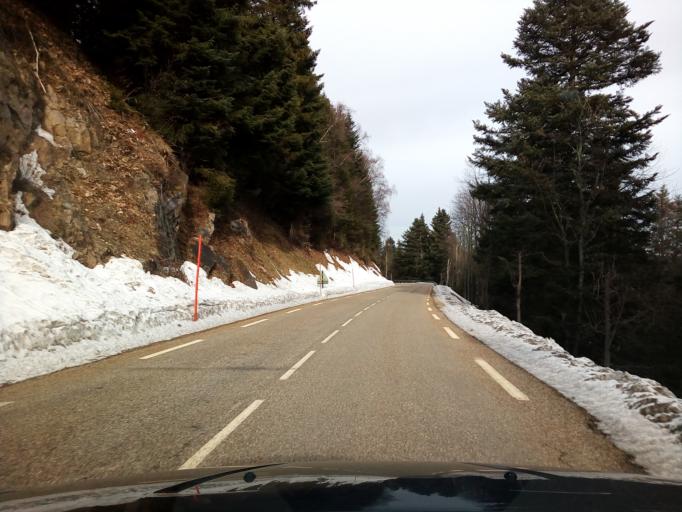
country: FR
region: Rhone-Alpes
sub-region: Departement de l'Isere
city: Revel
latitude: 45.1433
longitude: 5.8875
